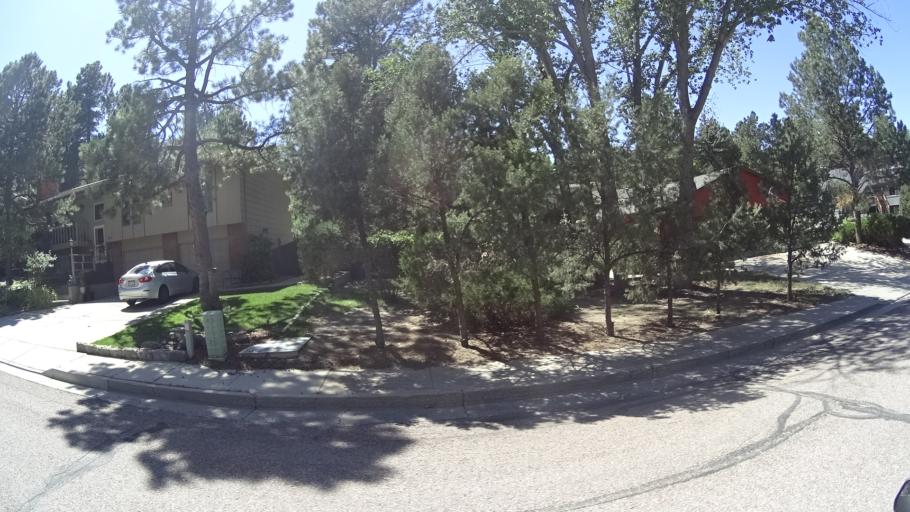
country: US
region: Colorado
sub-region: El Paso County
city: Colorado Springs
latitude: 38.9224
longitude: -104.8044
